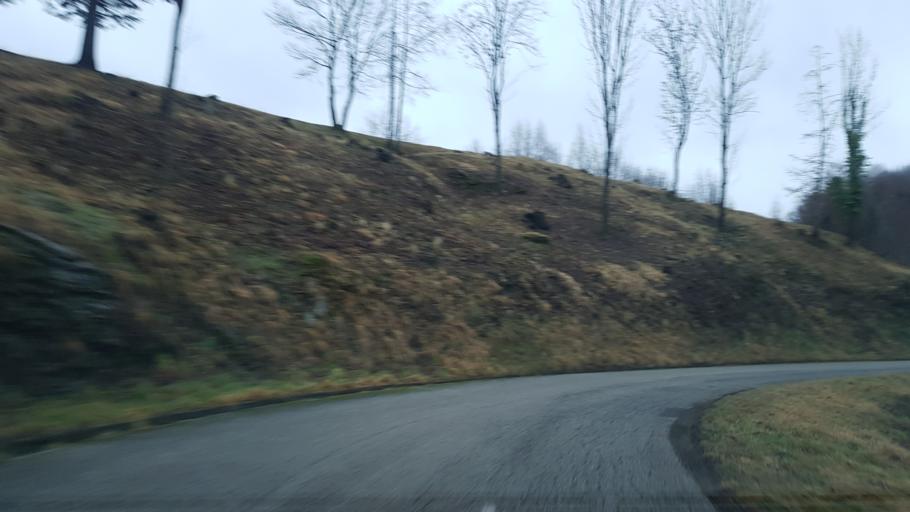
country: IT
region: Friuli Venezia Giulia
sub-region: Provincia di Udine
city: Stregna
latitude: 46.1214
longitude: 13.5986
